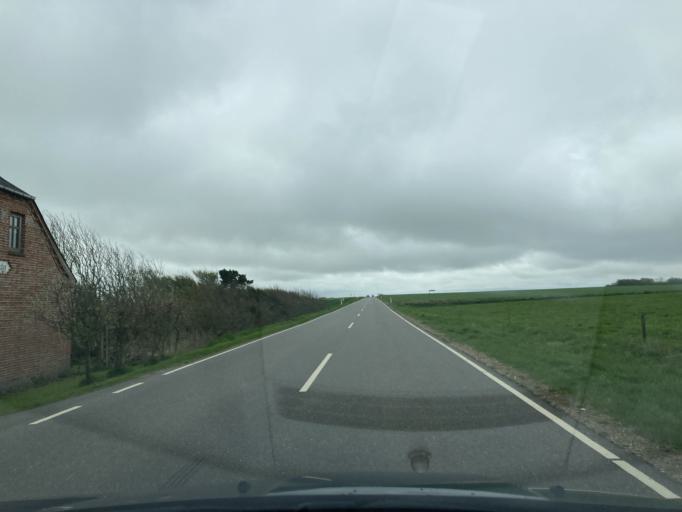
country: DK
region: North Denmark
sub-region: Thisted Kommune
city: Hurup
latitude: 56.8253
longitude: 8.3558
